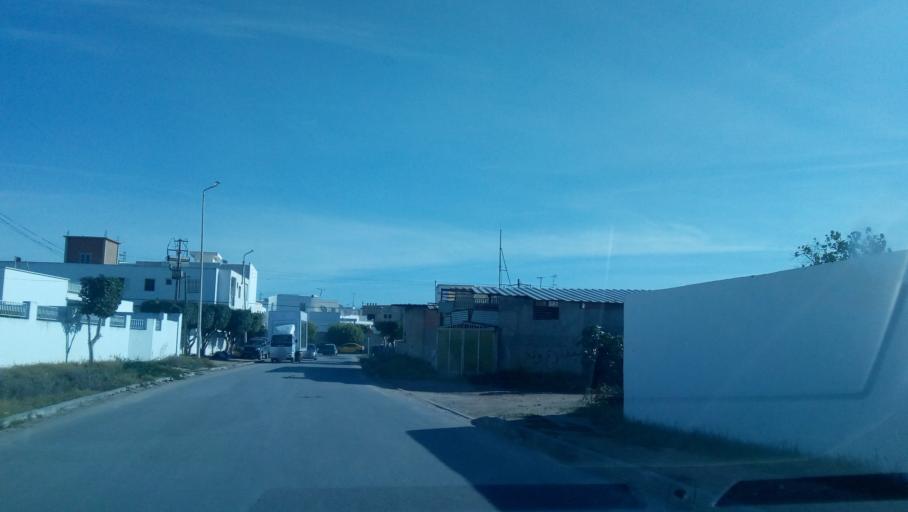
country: TN
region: Safaqis
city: Sfax
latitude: 34.7497
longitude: 10.7406
